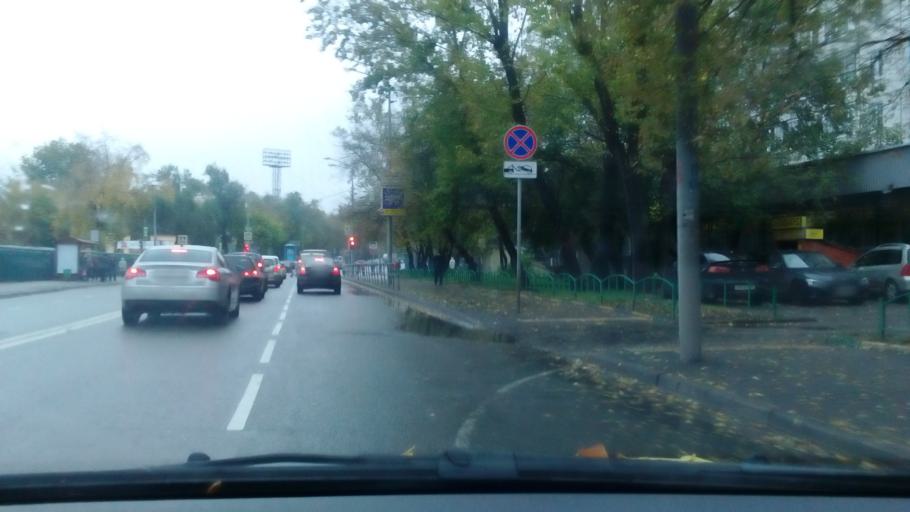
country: RU
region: Moscow
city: Mar'ina Roshcha
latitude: 55.8018
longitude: 37.5751
